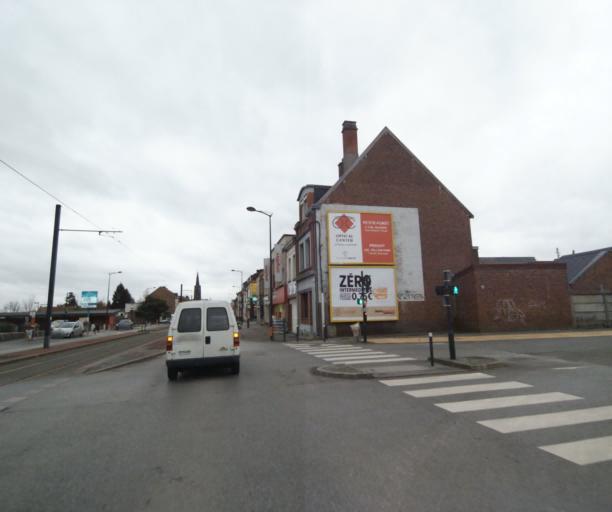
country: FR
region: Nord-Pas-de-Calais
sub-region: Departement du Nord
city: Anzin
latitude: 50.3756
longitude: 3.5172
